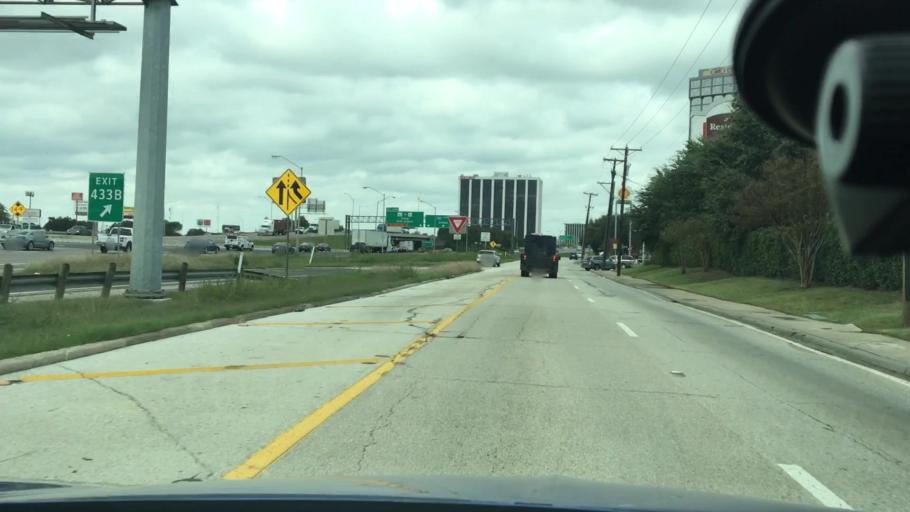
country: US
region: Texas
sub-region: Dallas County
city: Dallas
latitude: 32.8141
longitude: -96.8656
